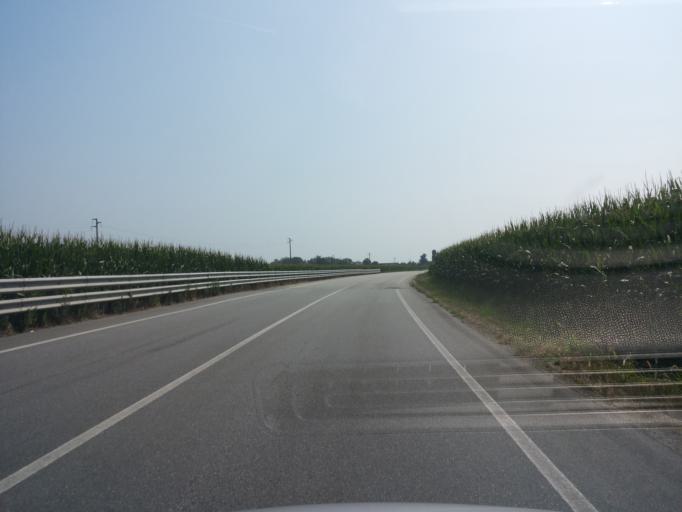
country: IT
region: Piedmont
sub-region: Provincia di Alessandria
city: Villanova Monferrato
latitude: 45.1609
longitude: 8.4682
